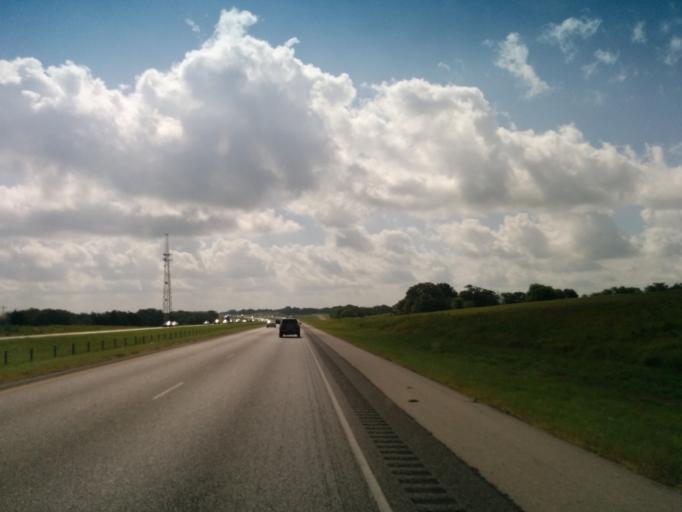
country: US
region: Texas
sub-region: Fayette County
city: Flatonia
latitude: 29.6929
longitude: -97.0163
